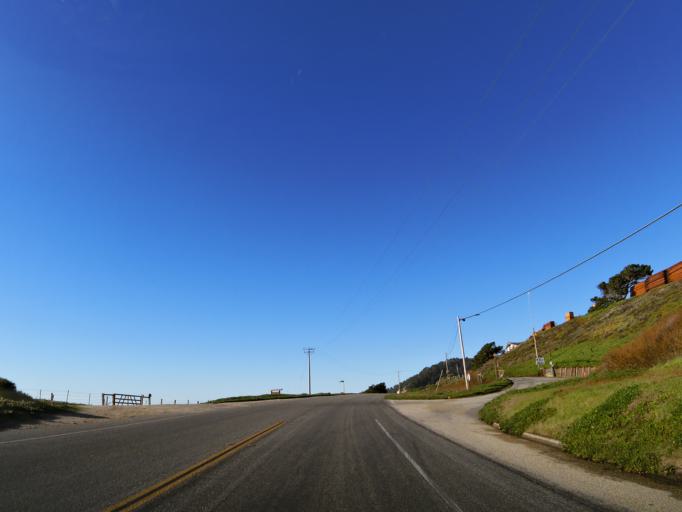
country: US
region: California
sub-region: Santa Cruz County
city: Bonny Doon
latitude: 37.0876
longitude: -122.2721
